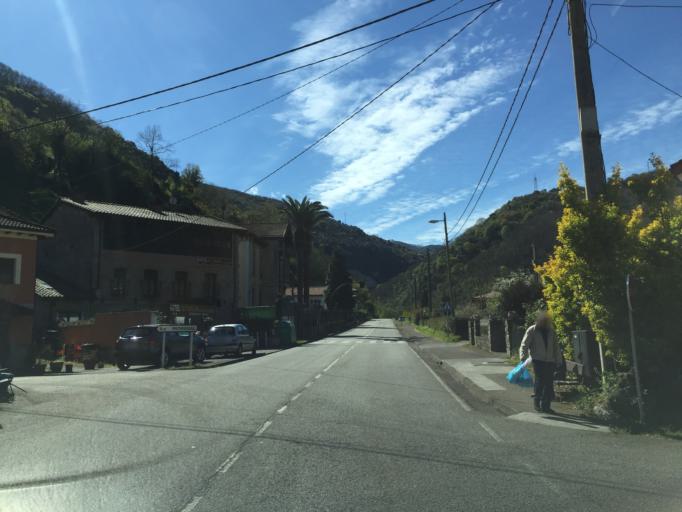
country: ES
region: Asturias
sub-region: Province of Asturias
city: Proaza
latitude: 43.3128
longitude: -5.9884
